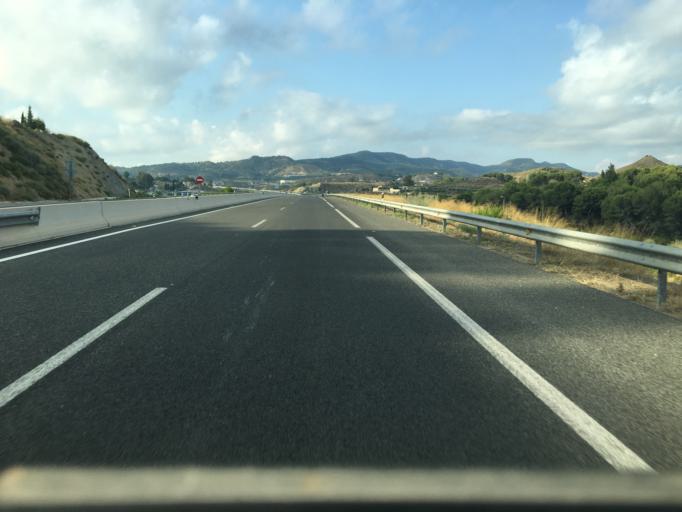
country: ES
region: Murcia
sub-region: Murcia
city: Beniel
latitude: 37.9802
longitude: -0.9748
